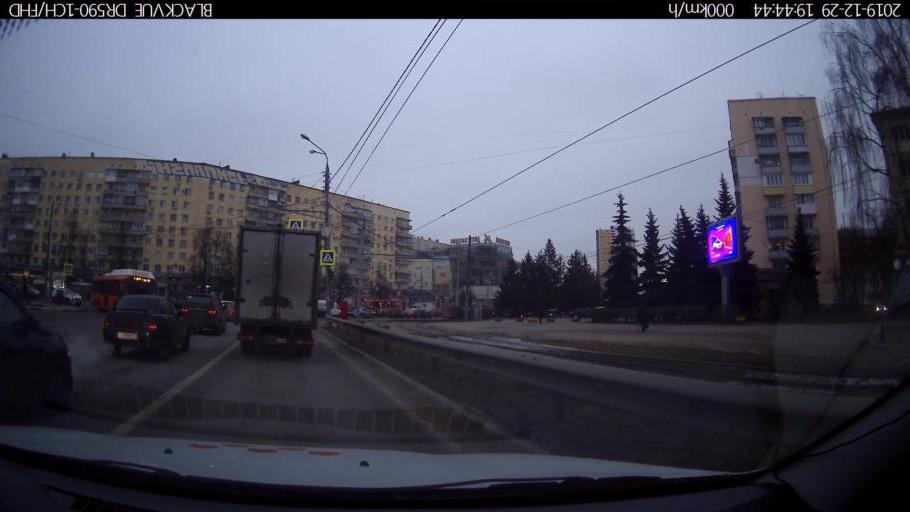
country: RU
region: Nizjnij Novgorod
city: Neklyudovo
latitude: 56.3490
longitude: 43.8673
